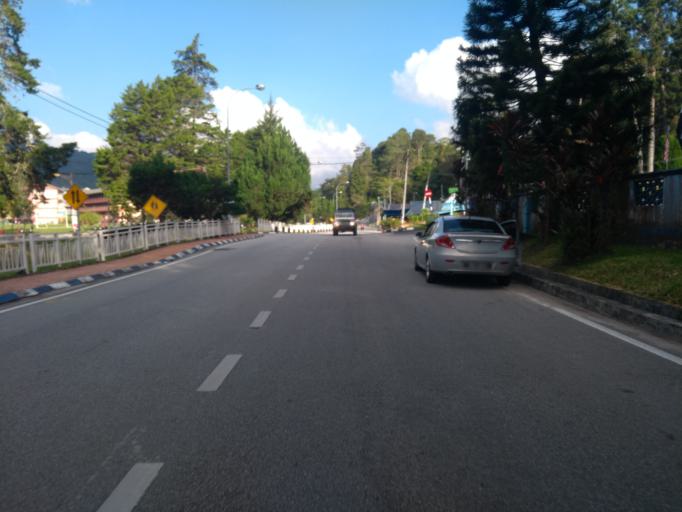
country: MY
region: Pahang
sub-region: Cameron Highlands
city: Tanah Rata
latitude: 4.4699
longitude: 101.3811
